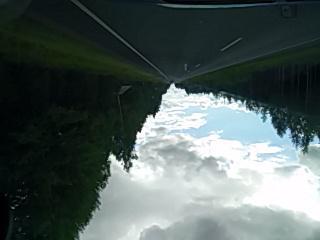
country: FI
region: Haeme
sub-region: Haemeenlinna
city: Renko
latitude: 60.8701
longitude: 24.2076
